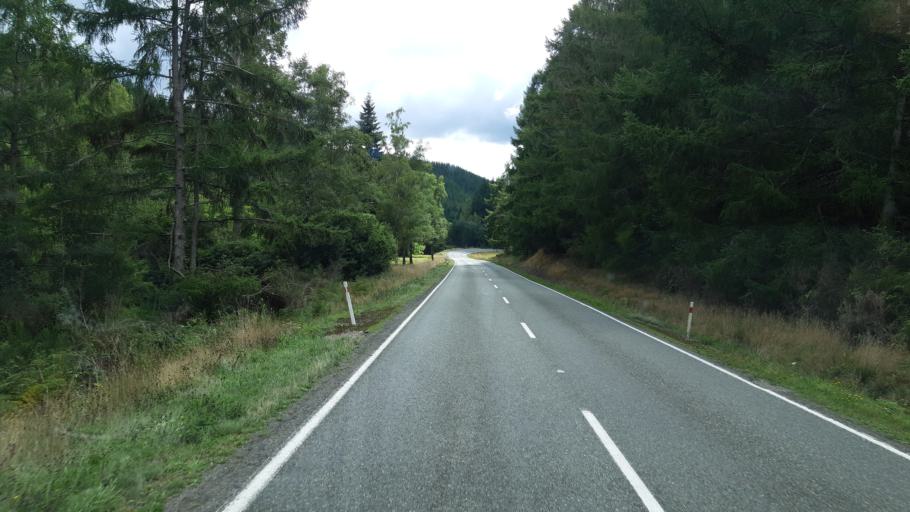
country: NZ
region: Tasman
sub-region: Tasman District
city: Wakefield
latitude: -41.6059
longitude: 172.7592
